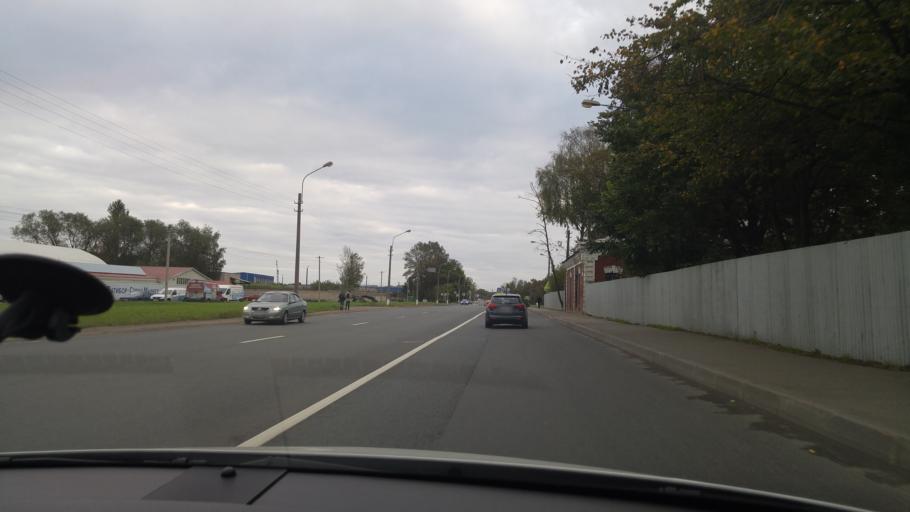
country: RU
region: St.-Petersburg
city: Kronshtadt
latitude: 60.0100
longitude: 29.7298
